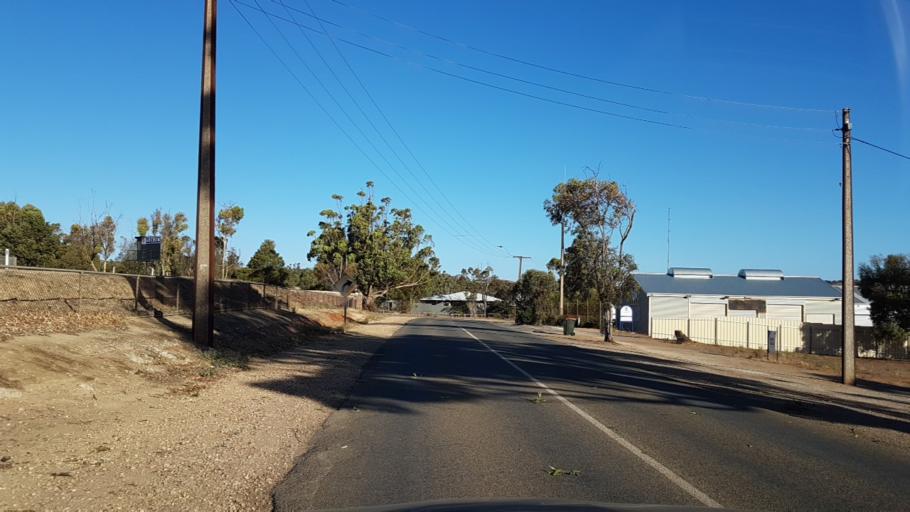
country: AU
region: South Australia
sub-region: Clare and Gilbert Valleys
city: Clare
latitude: -33.6769
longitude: 138.9404
